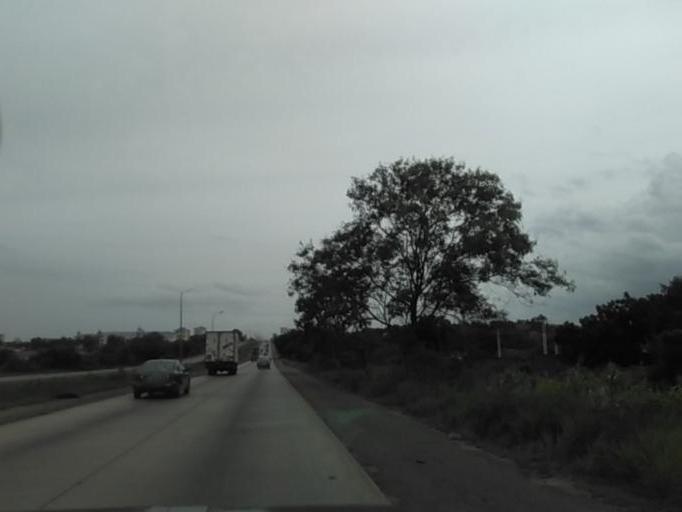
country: GH
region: Greater Accra
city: Medina Estates
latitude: 5.6287
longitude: -0.1594
